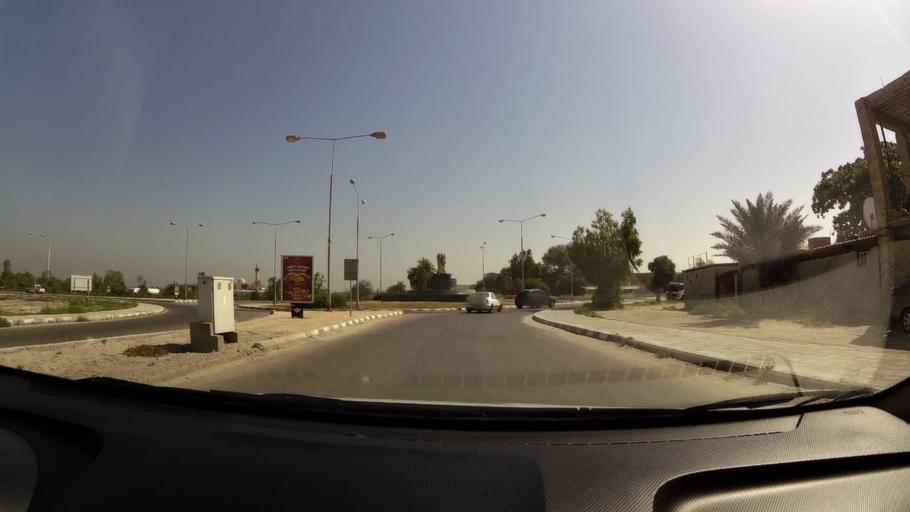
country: AE
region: Umm al Qaywayn
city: Umm al Qaywayn
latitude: 25.5844
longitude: 55.5688
